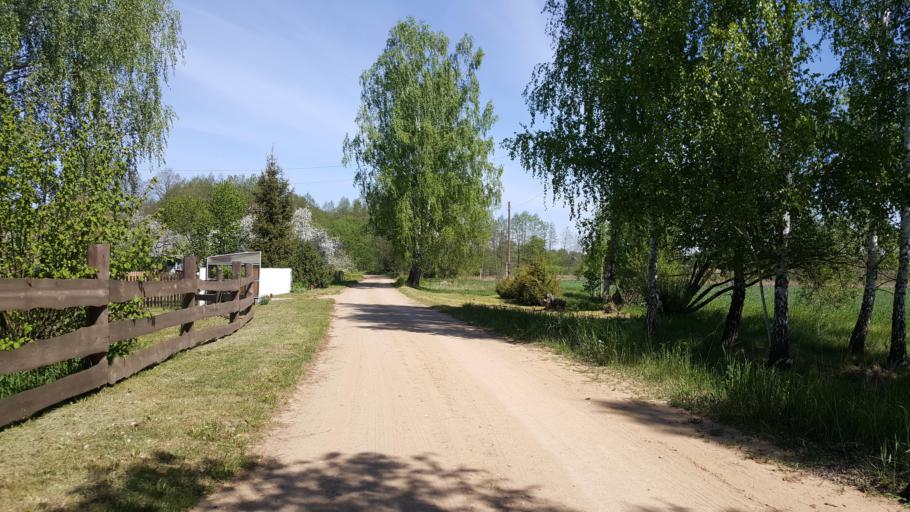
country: BY
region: Brest
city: Zhabinka
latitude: 52.3796
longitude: 24.0223
